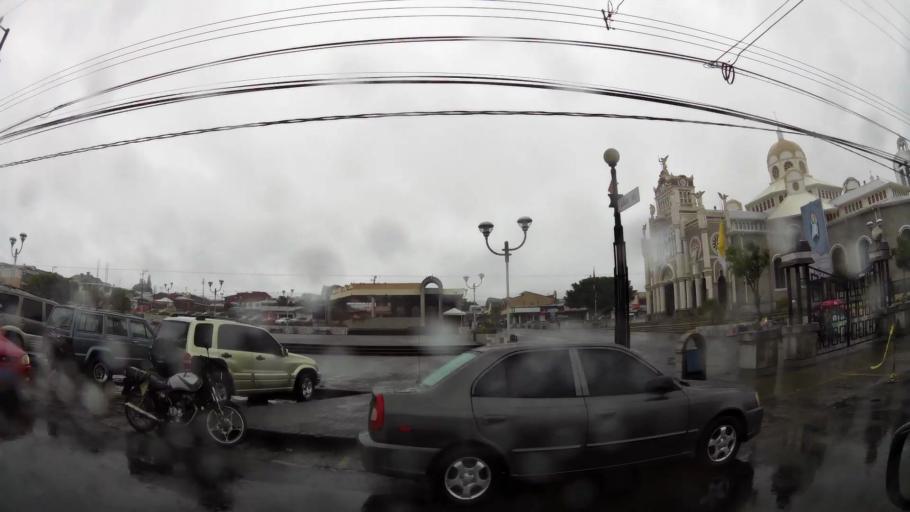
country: CR
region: Cartago
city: Cartago
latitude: 9.8638
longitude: -83.9134
